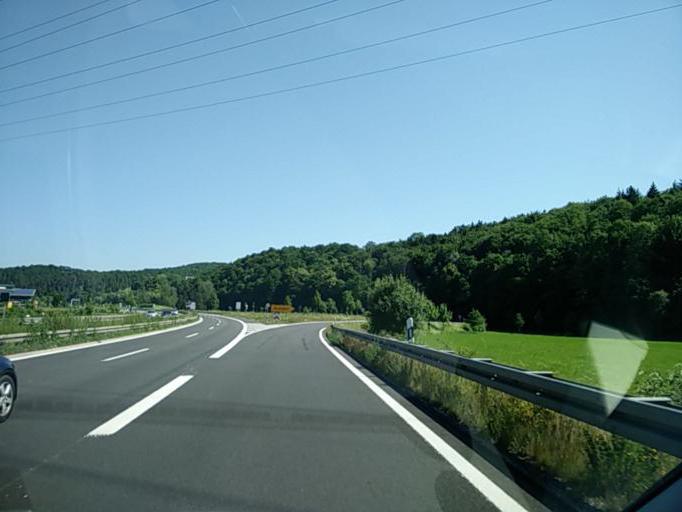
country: DE
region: Baden-Wuerttemberg
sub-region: Tuebingen Region
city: Dusslingen
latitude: 48.4841
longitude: 9.0681
